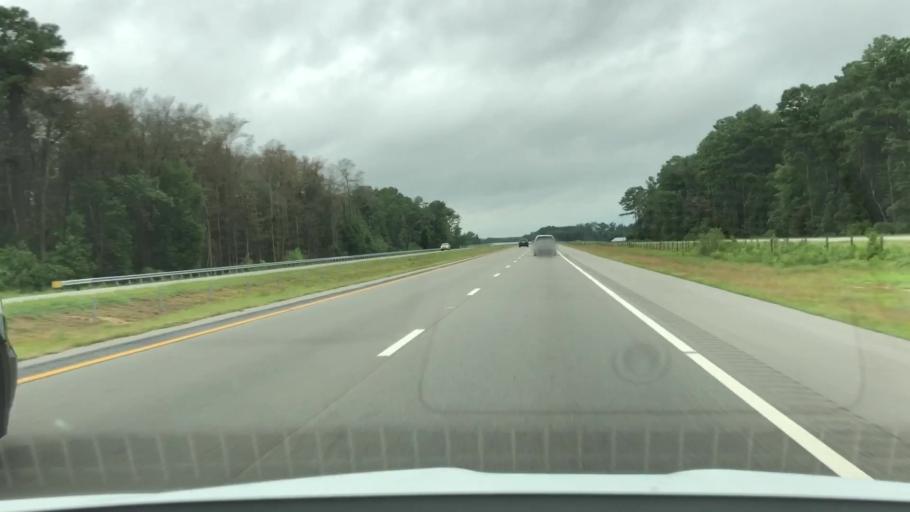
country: US
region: North Carolina
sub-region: Wayne County
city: Elroy
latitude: 35.3493
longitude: -77.8471
